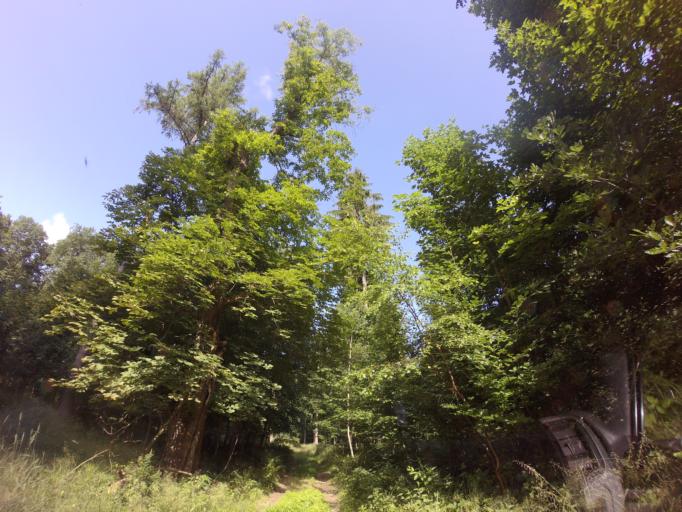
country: PL
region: West Pomeranian Voivodeship
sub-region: Powiat choszczenski
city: Krzecin
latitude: 52.9966
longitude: 15.5110
